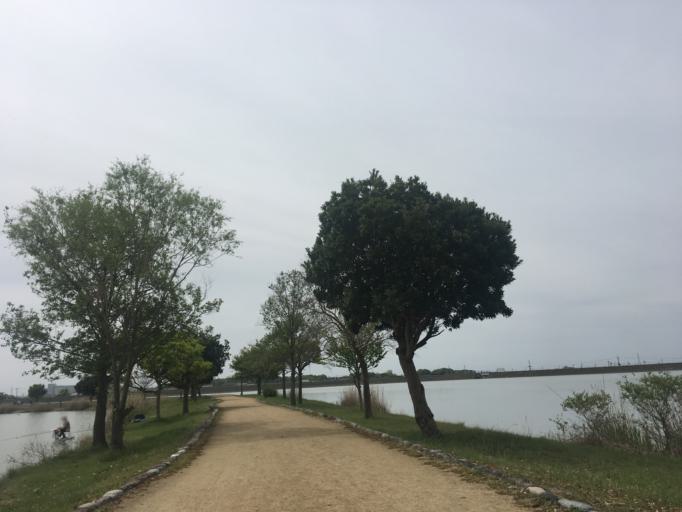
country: JP
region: Hyogo
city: Miki
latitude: 34.7652
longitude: 134.9229
